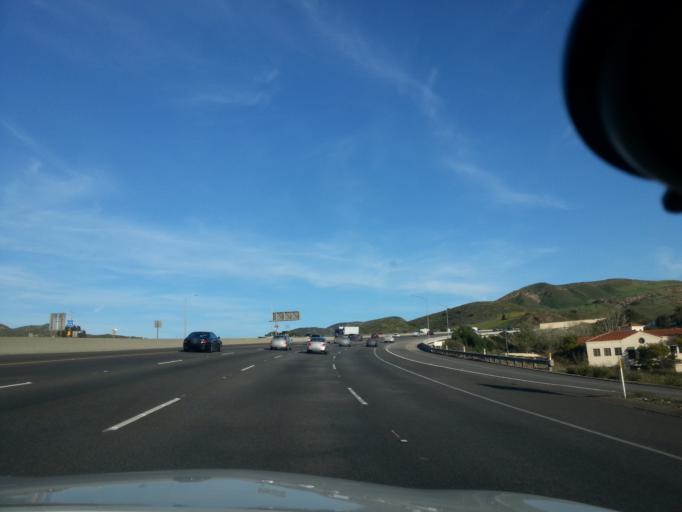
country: US
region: California
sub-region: Ventura County
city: Casa Conejo
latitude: 34.2054
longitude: -118.9852
